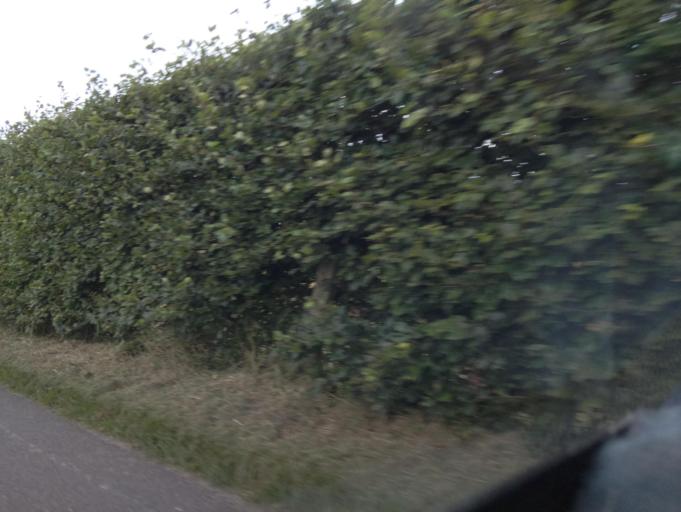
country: GB
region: Scotland
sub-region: Fife
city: Saint Andrews
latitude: 56.3182
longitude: -2.7798
